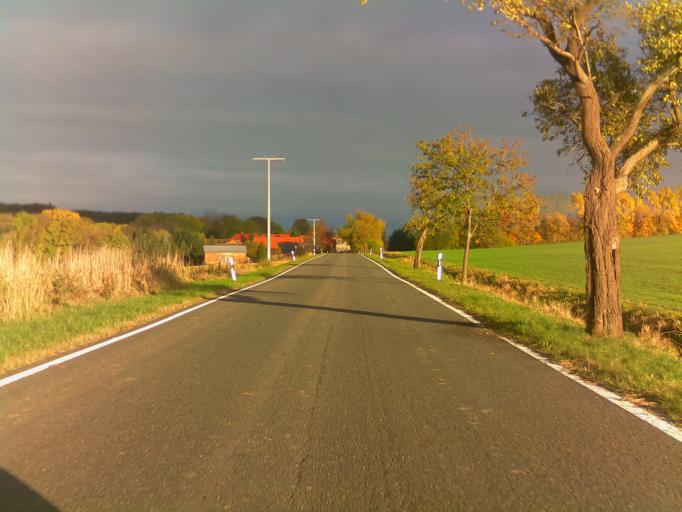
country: DE
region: Thuringia
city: Blankenhain
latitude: 50.8415
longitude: 11.3636
